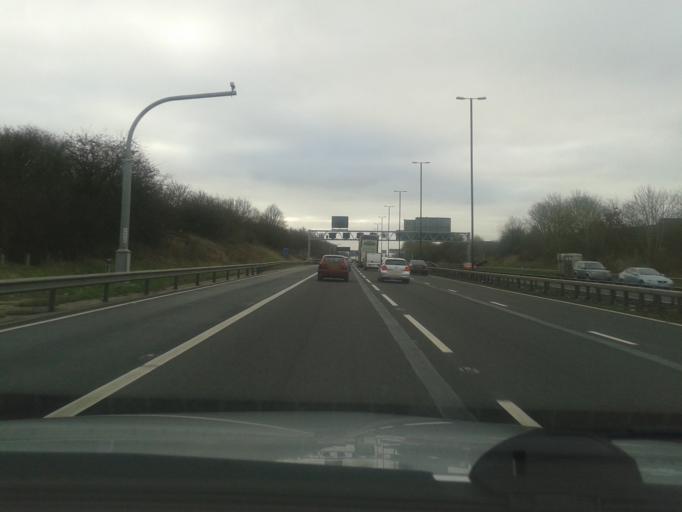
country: GB
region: England
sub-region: South Gloucestershire
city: Stoke Gifford
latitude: 51.5322
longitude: -2.5340
